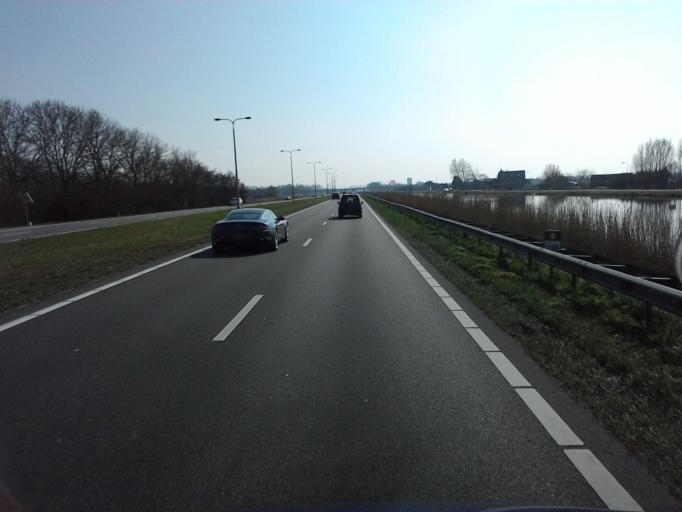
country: NL
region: North Holland
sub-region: Gemeente Zaanstad
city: Zaanstad
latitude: 52.4834
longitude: 4.7710
